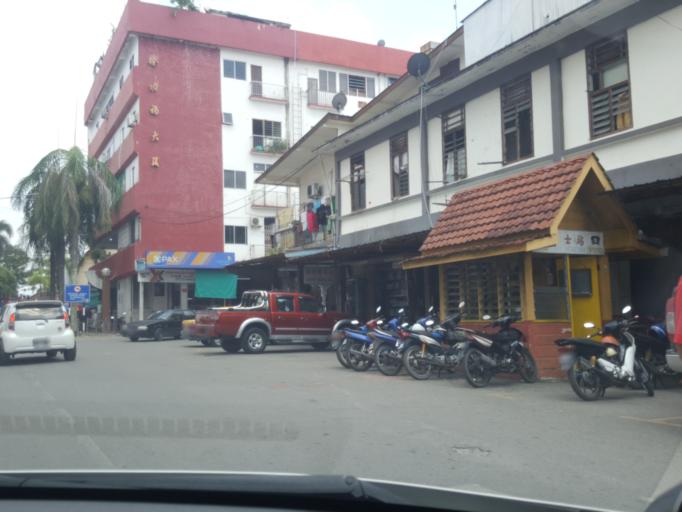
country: MY
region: Sarawak
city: Sarikei
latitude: 2.1320
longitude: 111.5213
